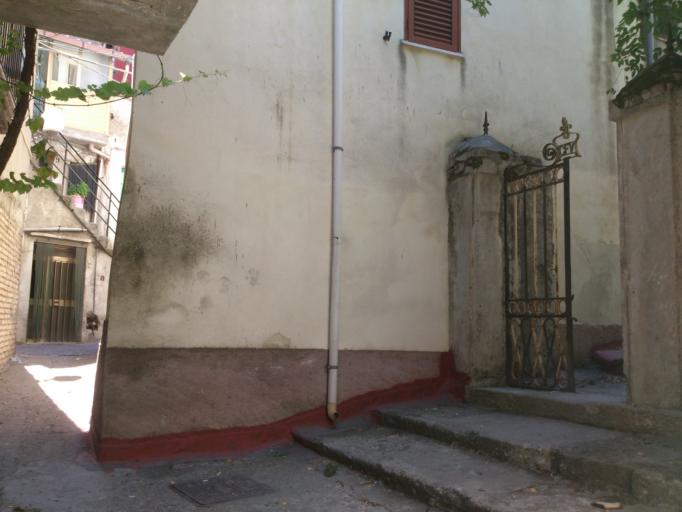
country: IT
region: Calabria
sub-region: Provincia di Reggio Calabria
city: Pazzano
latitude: 38.4766
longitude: 16.4515
